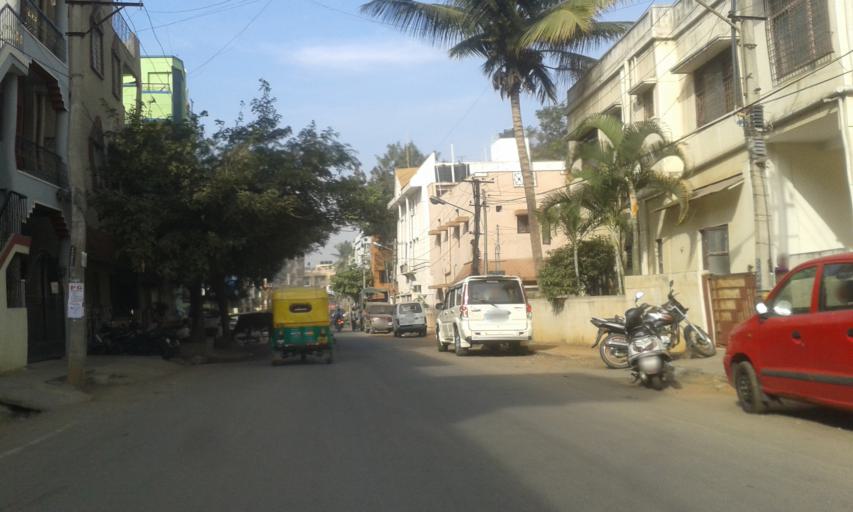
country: IN
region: Karnataka
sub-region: Bangalore Urban
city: Bangalore
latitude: 12.9417
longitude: 77.6172
